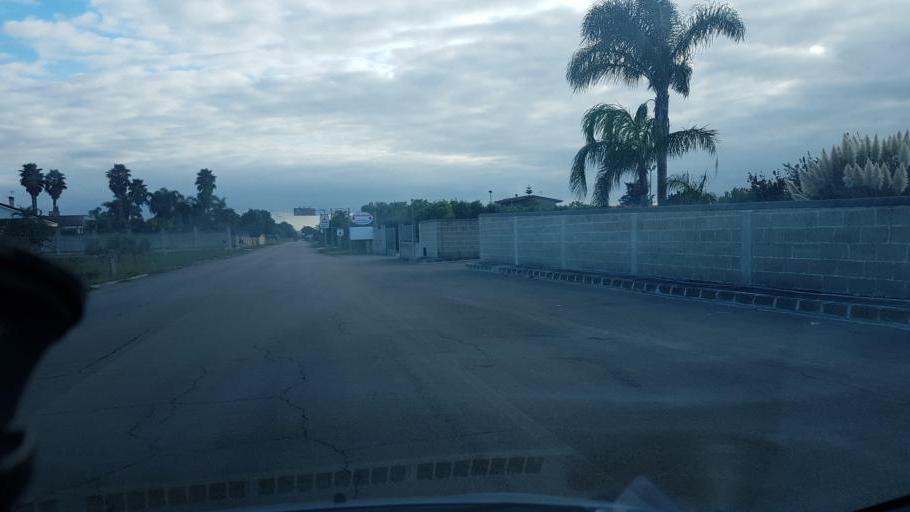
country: IT
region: Apulia
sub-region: Provincia di Lecce
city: Veglie
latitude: 40.3487
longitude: 17.9689
